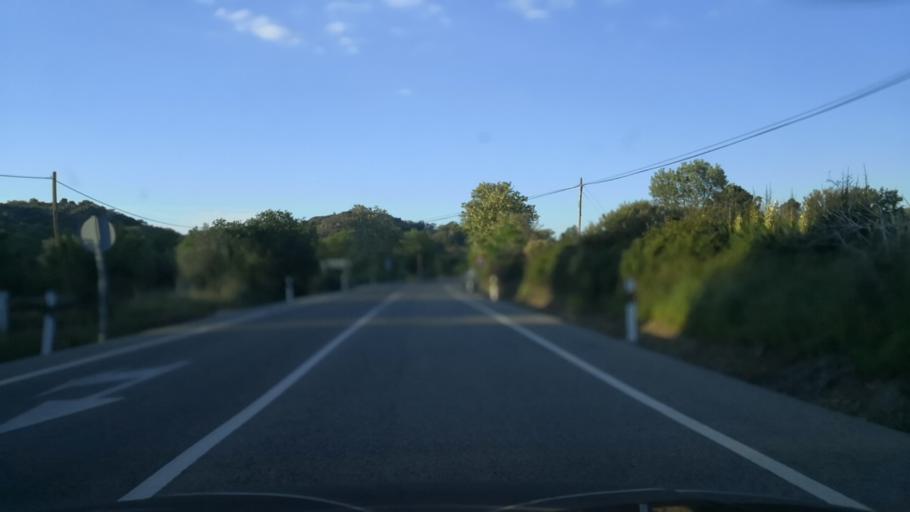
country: ES
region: Extremadura
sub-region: Provincia de Caceres
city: Valencia de Alcantara
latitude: 39.3643
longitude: -7.2723
